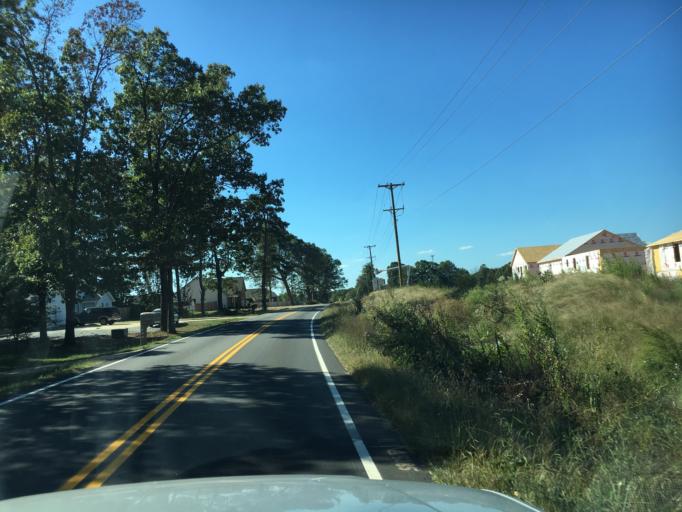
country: US
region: South Carolina
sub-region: Spartanburg County
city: Duncan
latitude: 34.8943
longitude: -82.1214
